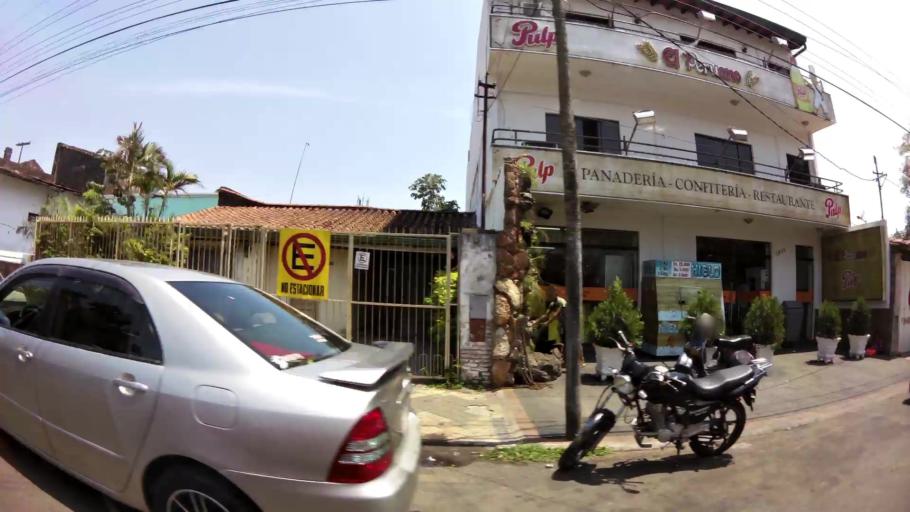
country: PY
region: Asuncion
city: Asuncion
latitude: -25.2970
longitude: -57.6445
